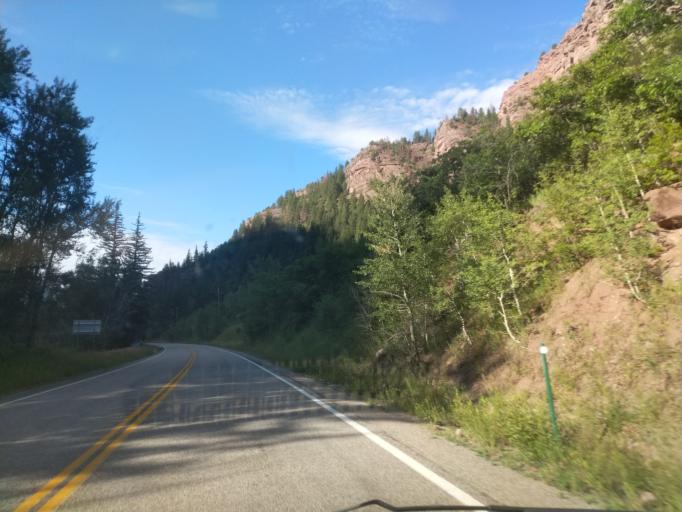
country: US
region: Colorado
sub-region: Garfield County
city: Carbondale
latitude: 39.2016
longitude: -107.2322
